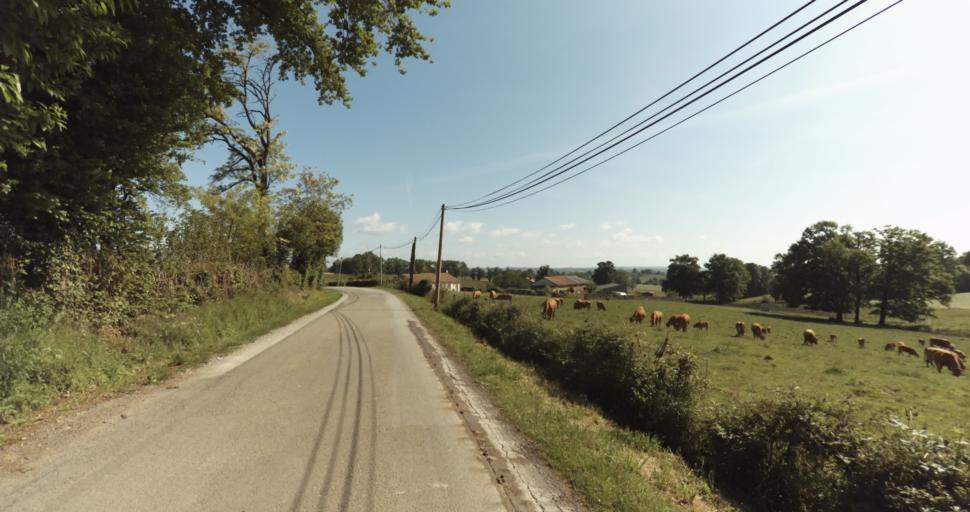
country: FR
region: Limousin
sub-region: Departement de la Haute-Vienne
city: Solignac
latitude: 45.7247
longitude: 1.2691
